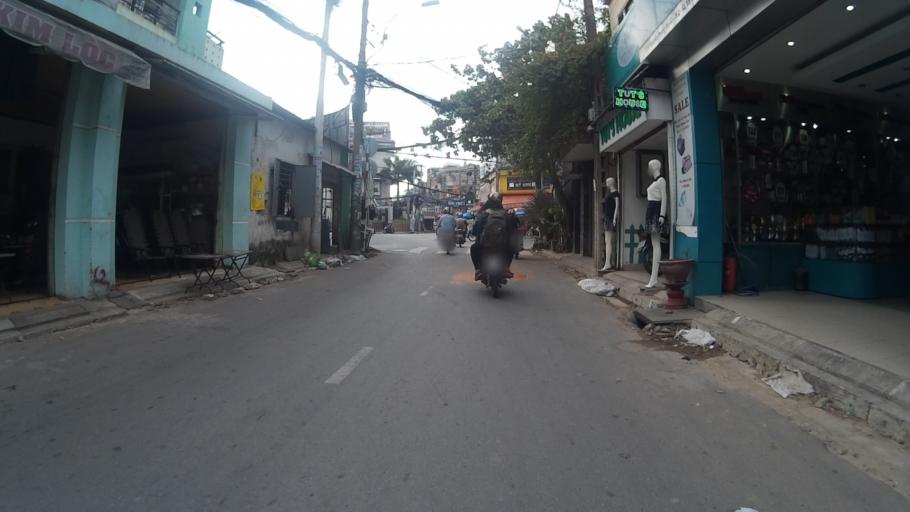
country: VN
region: Ho Chi Minh City
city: Quan Phu Nhuan
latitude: 10.7989
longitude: 106.6629
